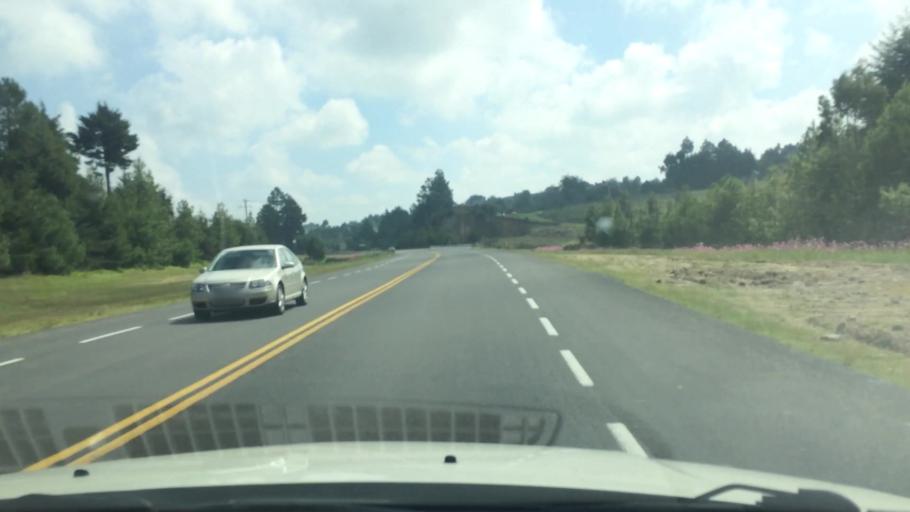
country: MX
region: Mexico
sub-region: Villa Victoria
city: Colonia Doctor Gustavo Baz
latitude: 19.3577
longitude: -99.9598
